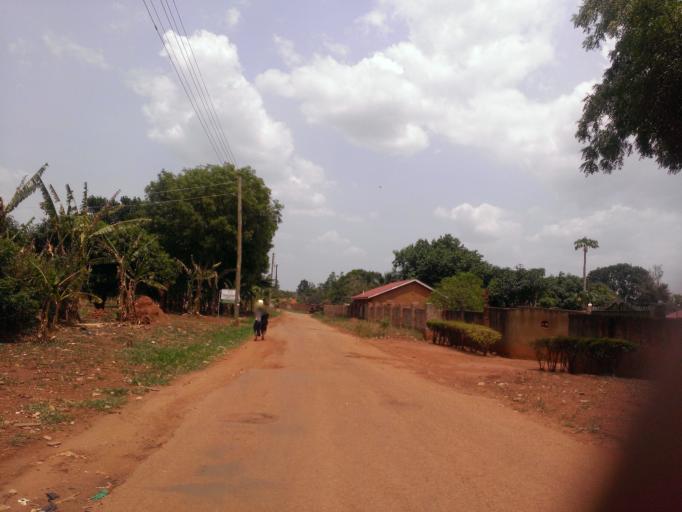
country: UG
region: Northern Region
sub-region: Gulu District
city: Gulu
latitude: 2.7815
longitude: 32.3017
